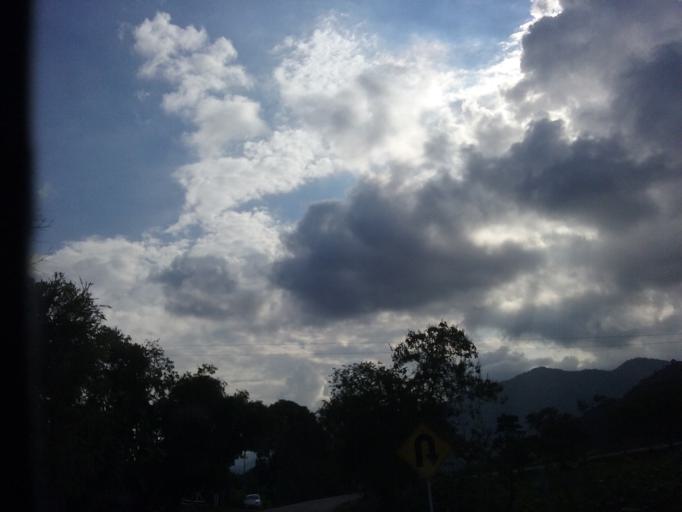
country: CO
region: Tolima
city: Libano
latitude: 4.8914
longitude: -75.0345
